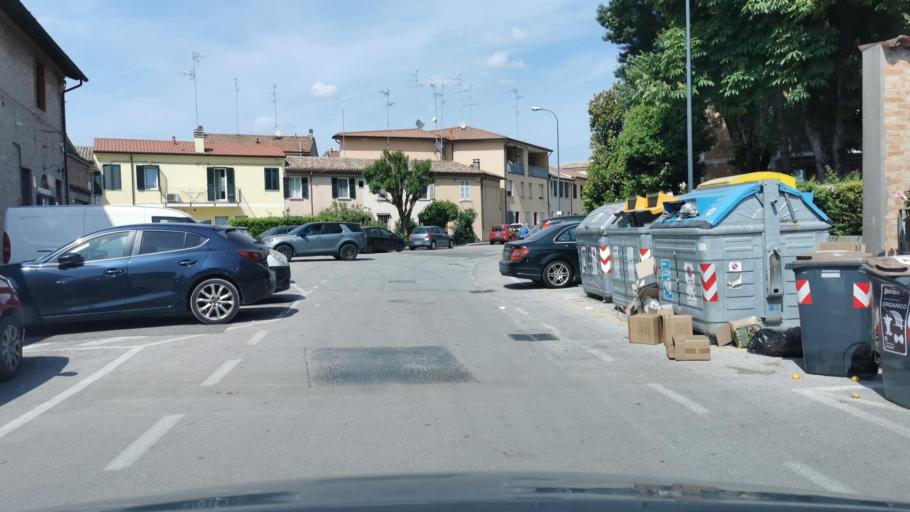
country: IT
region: Emilia-Romagna
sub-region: Provincia di Ravenna
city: Ravenna
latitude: 44.4107
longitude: 12.1992
